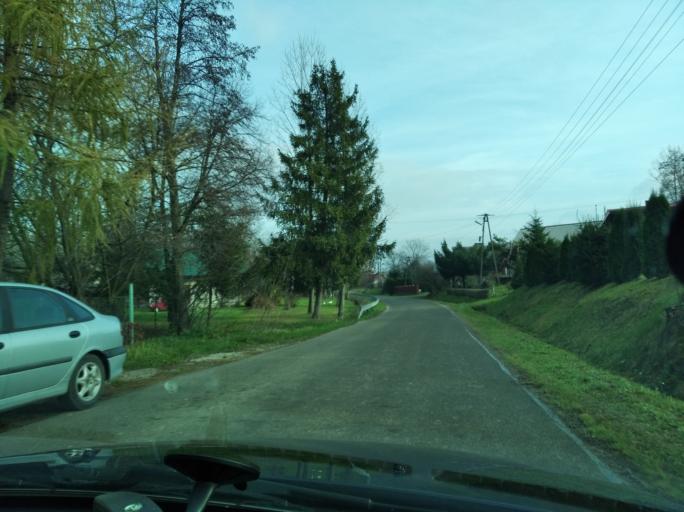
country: PL
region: Subcarpathian Voivodeship
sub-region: Powiat przeworski
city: Siedleczka
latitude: 49.9659
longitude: 22.3671
